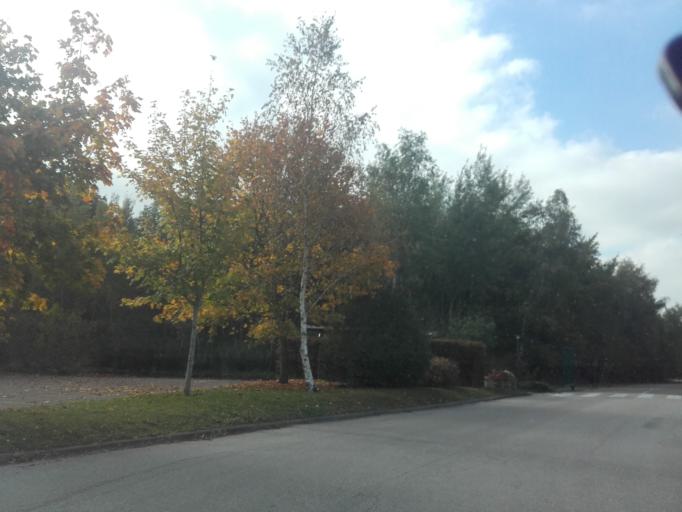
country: FR
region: Bourgogne
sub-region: Departement de Saone-et-Loire
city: Fontaines
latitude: 46.8863
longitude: 4.7857
